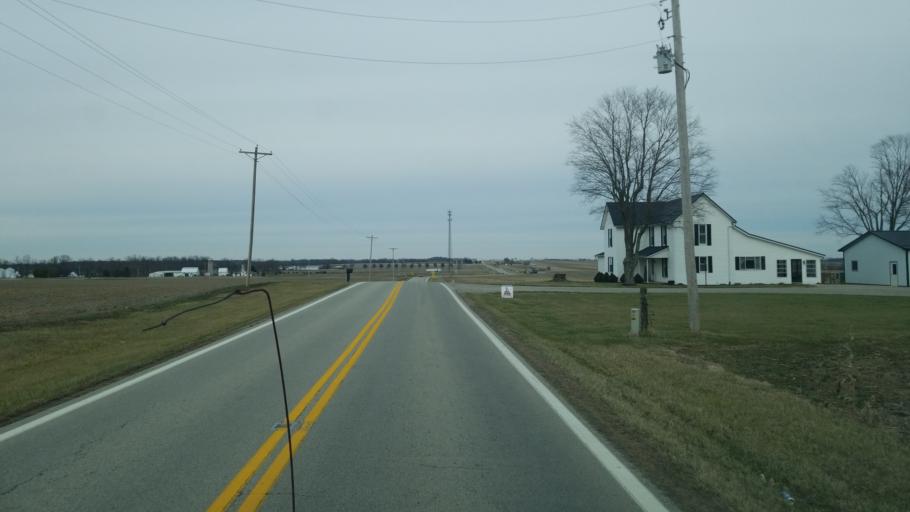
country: US
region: Ohio
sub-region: Ross County
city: Frankfort
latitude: 39.4410
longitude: -83.2206
